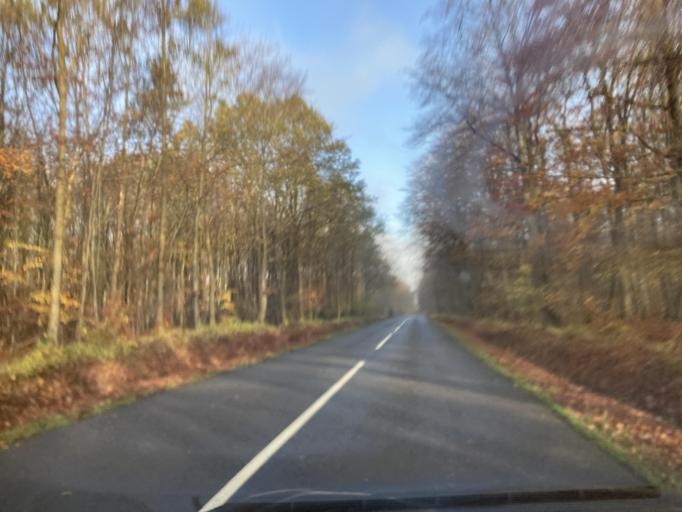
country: DK
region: Zealand
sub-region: Lolland Kommune
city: Rodby
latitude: 54.7639
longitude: 11.3585
